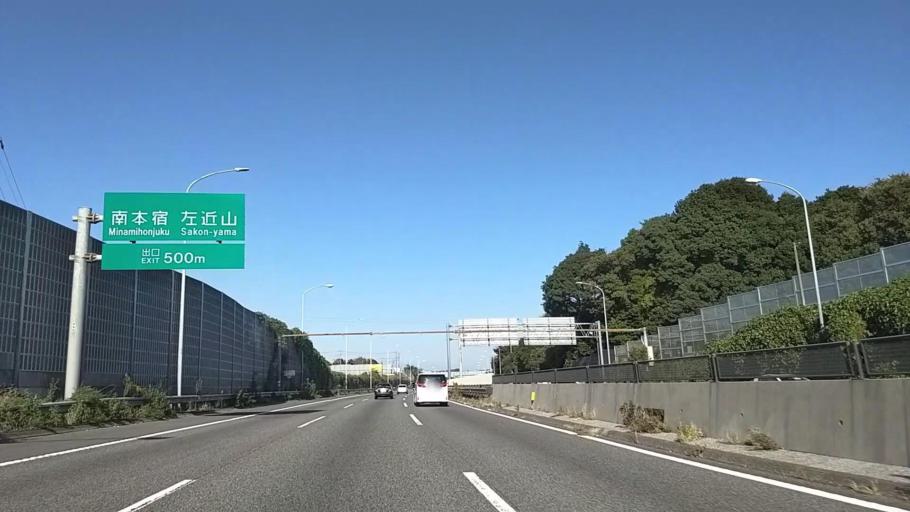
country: JP
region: Kanagawa
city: Yokohama
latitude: 35.4574
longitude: 139.5477
